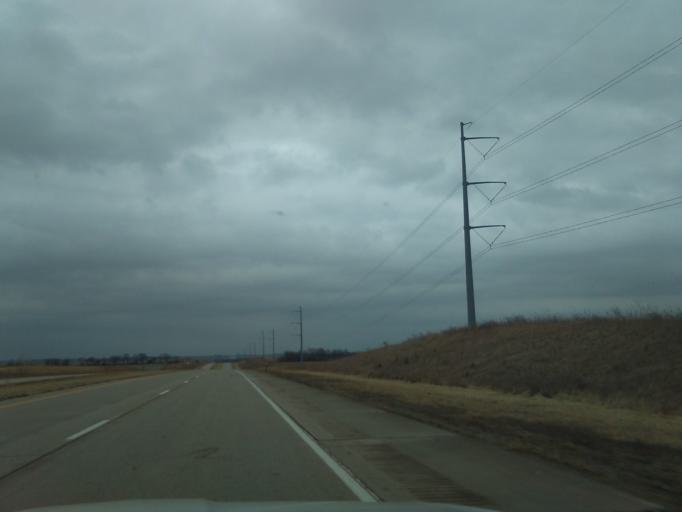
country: US
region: Nebraska
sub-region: Otoe County
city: Syracuse
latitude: 40.6755
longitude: -96.0679
